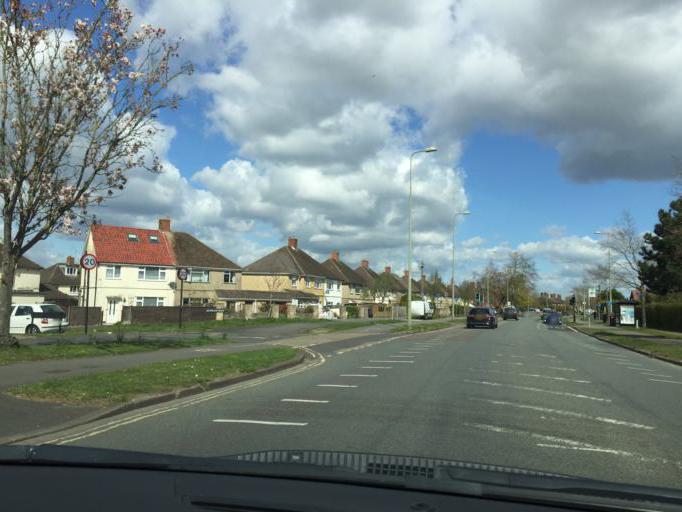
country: GB
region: England
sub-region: Oxfordshire
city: Oxford
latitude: 51.7619
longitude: -1.2357
